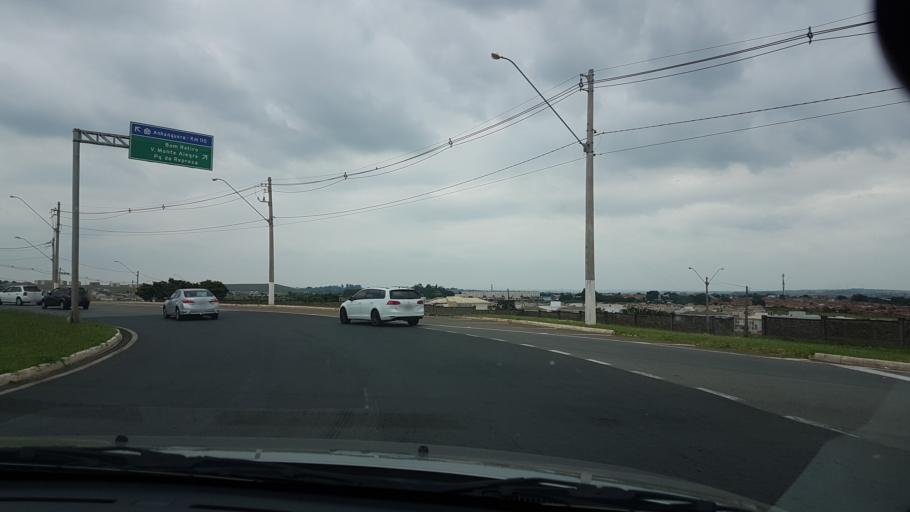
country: BR
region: Sao Paulo
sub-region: Paulinia
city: Paulinia
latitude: -22.7879
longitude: -47.1667
